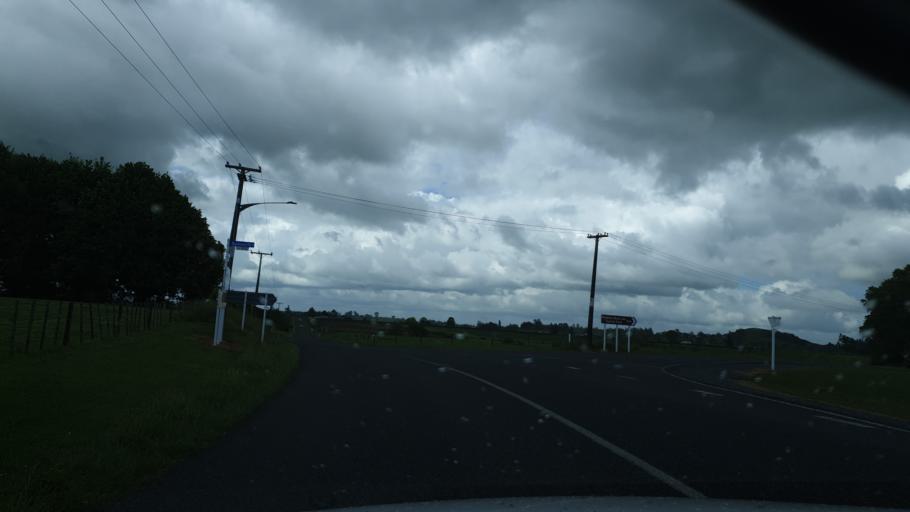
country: NZ
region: Waikato
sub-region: Matamata-Piako District
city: Matamata
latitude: -37.8735
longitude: 175.7248
